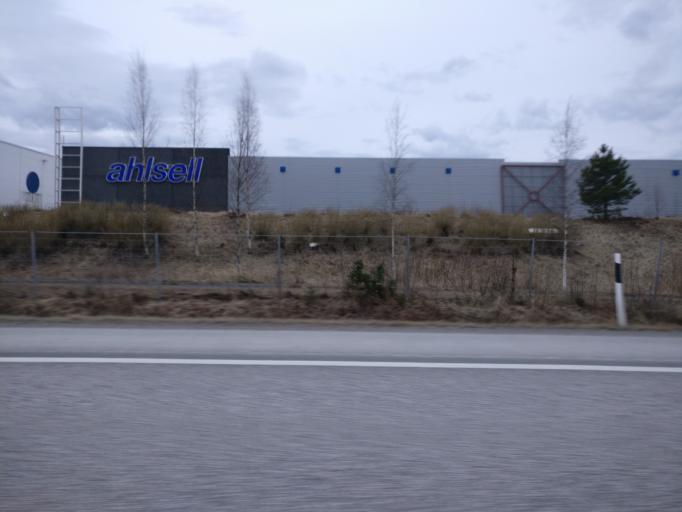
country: FI
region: Uusimaa
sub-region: Helsinki
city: Hyvinge
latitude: 60.5736
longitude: 24.8118
